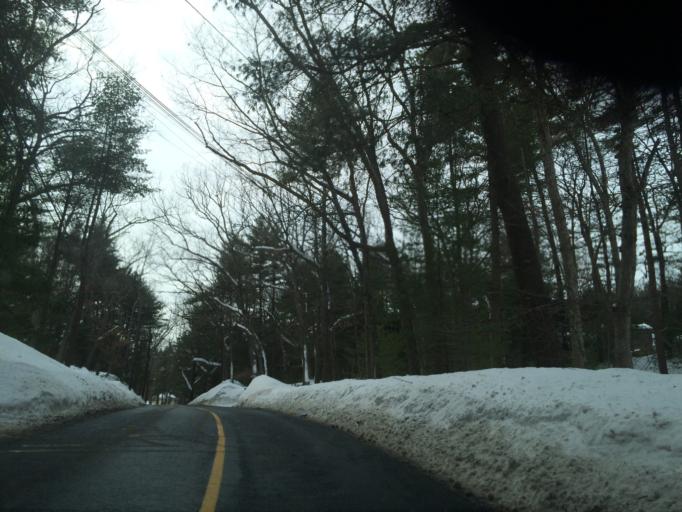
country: US
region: Massachusetts
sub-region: Middlesex County
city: Weston
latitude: 42.3857
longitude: -71.3082
